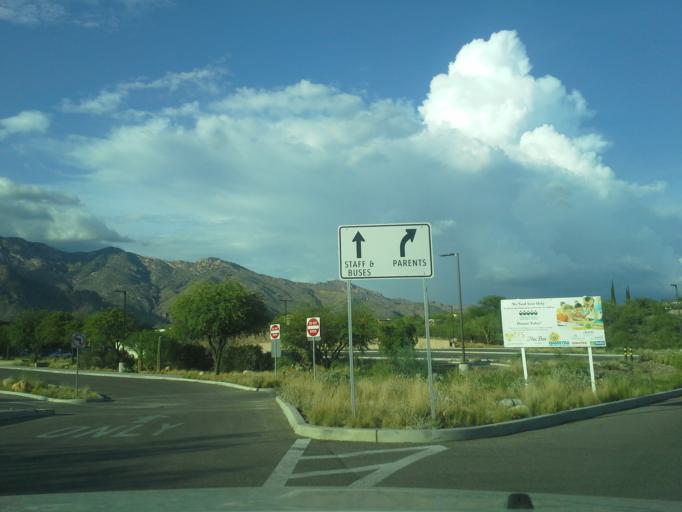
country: US
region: Arizona
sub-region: Pima County
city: Catalina Foothills
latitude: 32.3089
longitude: -110.8800
